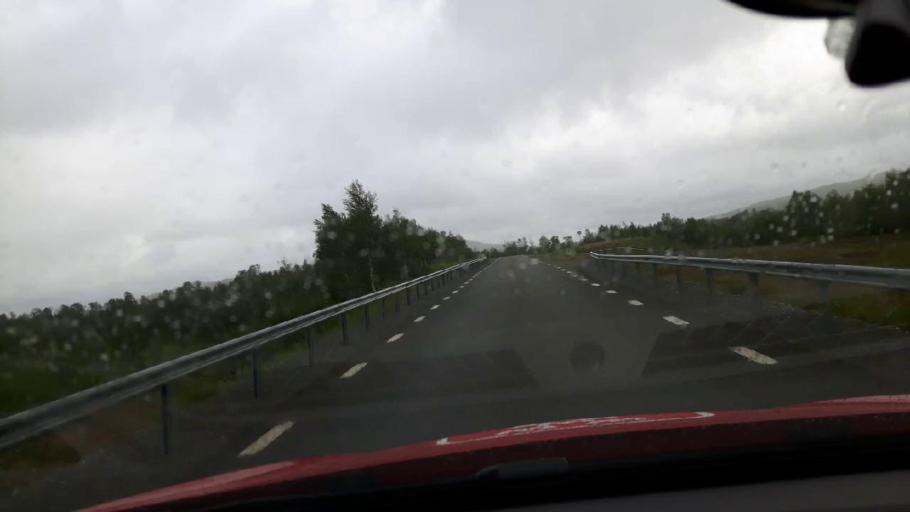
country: NO
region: Nord-Trondelag
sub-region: Meraker
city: Meraker
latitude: 63.1764
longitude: 12.3750
